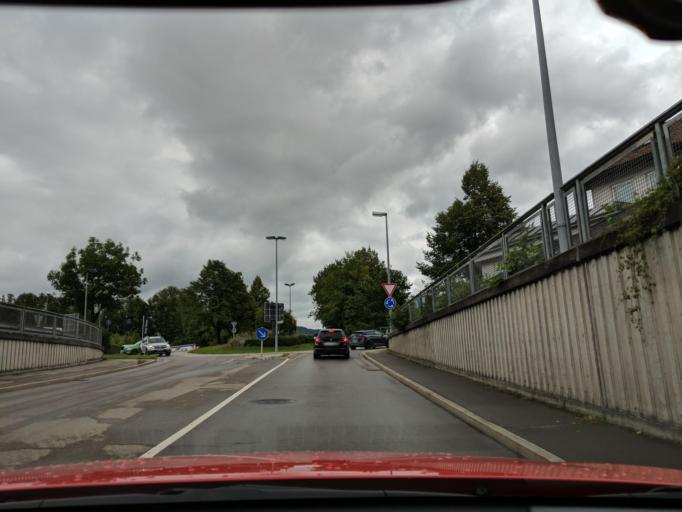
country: DE
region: Bavaria
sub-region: Swabia
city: Immenstadt im Allgau
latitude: 47.5542
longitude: 10.2311
